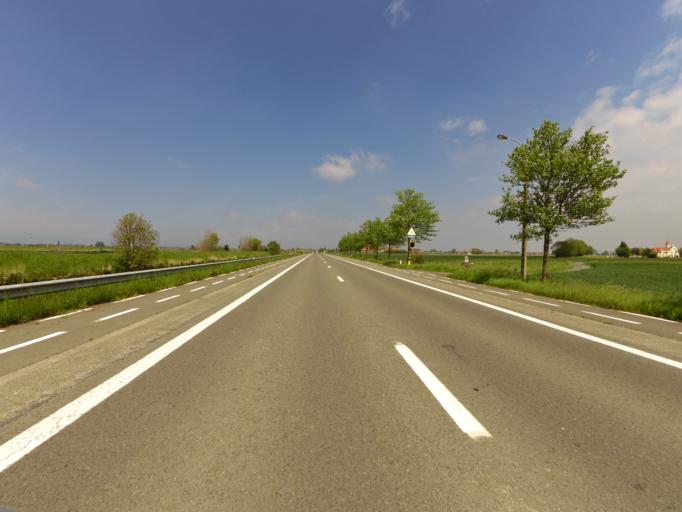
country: BE
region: Flanders
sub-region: Provincie West-Vlaanderen
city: Veurne
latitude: 51.0835
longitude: 2.6722
